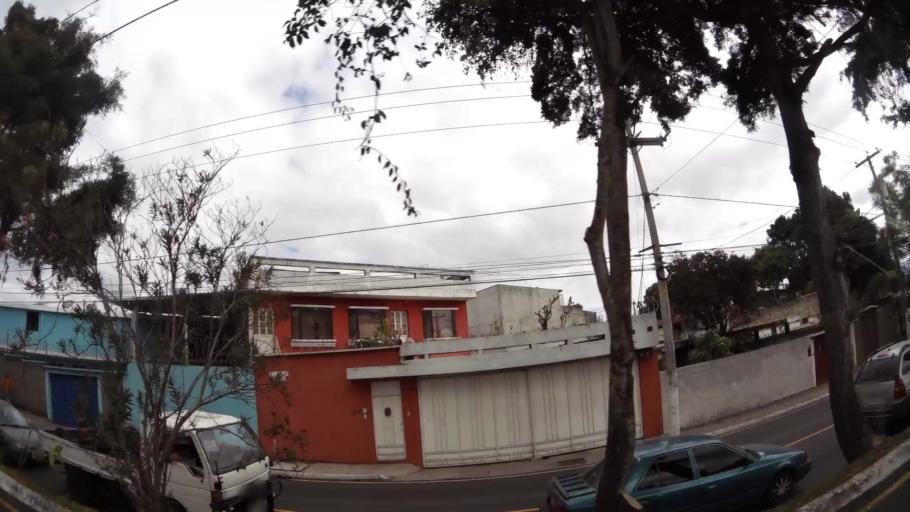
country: GT
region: Guatemala
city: Guatemala City
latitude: 14.6356
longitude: -90.5500
